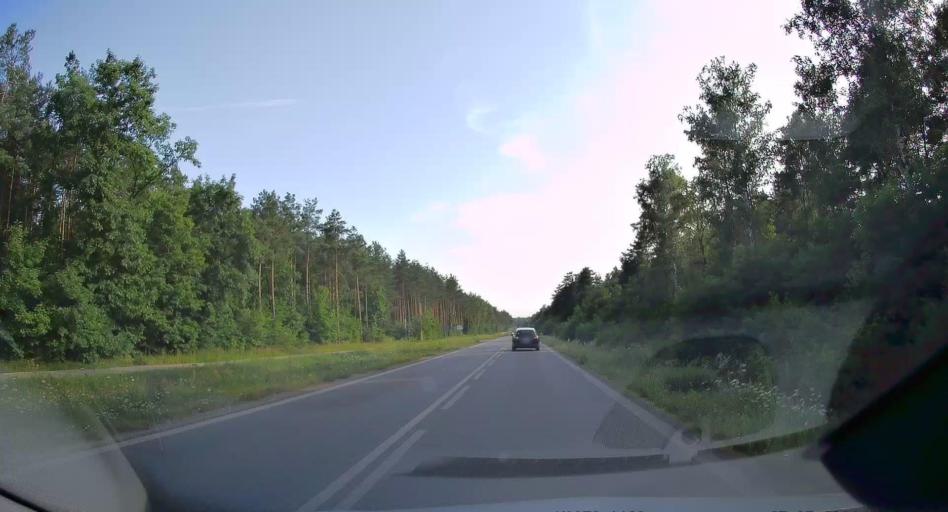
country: PL
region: Swietokrzyskie
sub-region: Powiat konecki
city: Konskie
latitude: 51.1269
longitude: 20.3587
